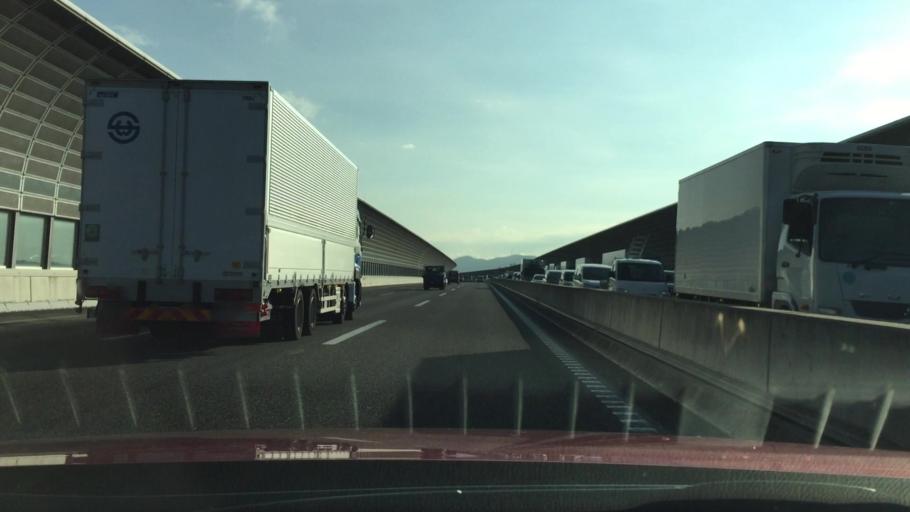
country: JP
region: Osaka
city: Neyagawa
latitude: 34.7451
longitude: 135.6226
